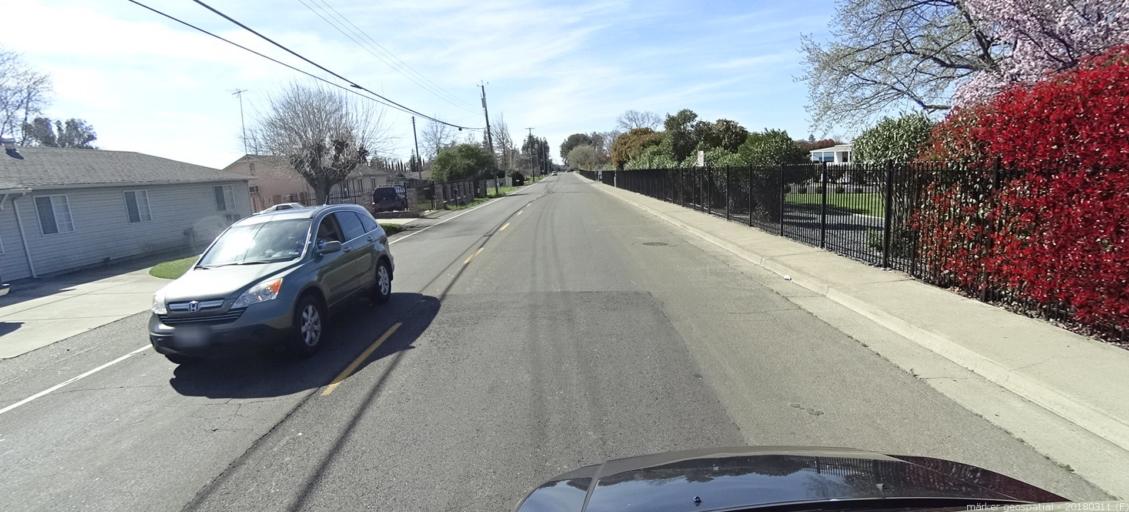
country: US
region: California
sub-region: Sacramento County
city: Florin
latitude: 38.4888
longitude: -121.4295
